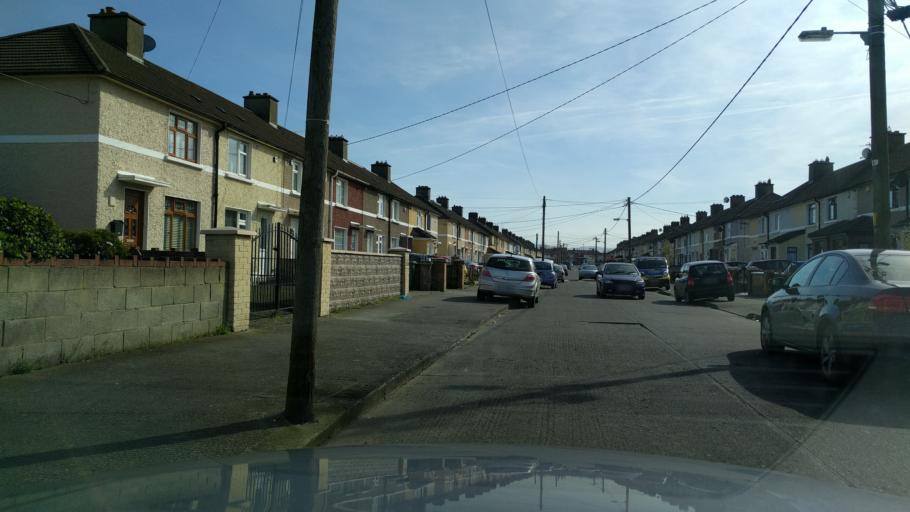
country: IE
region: Leinster
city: Chapelizod
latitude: 53.3414
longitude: -6.3511
